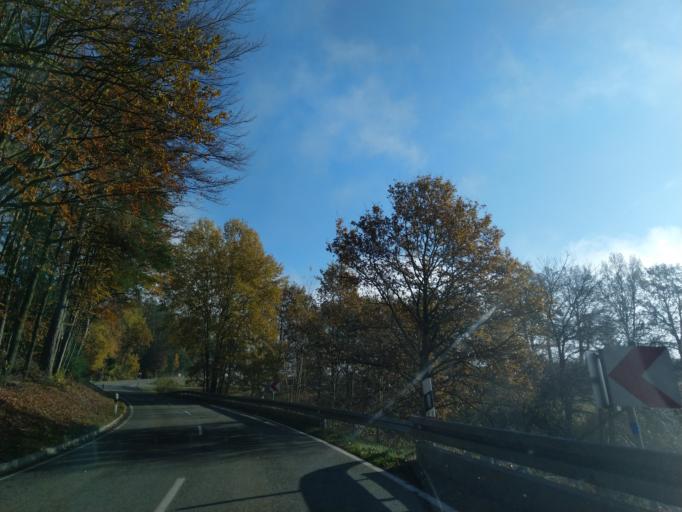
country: DE
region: Bavaria
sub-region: Lower Bavaria
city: Aussernzell
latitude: 48.7277
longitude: 13.1890
